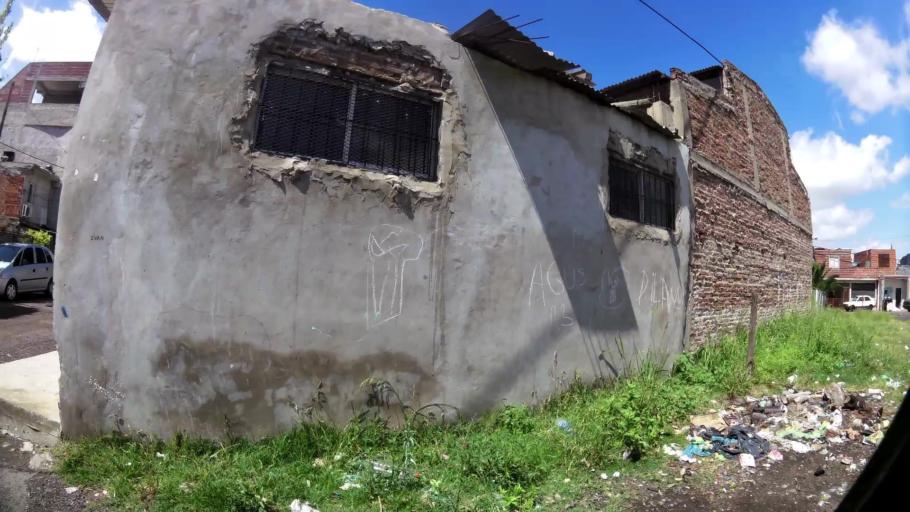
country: AR
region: Buenos Aires
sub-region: Partido de Lanus
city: Lanus
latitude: -34.6657
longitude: -58.4206
